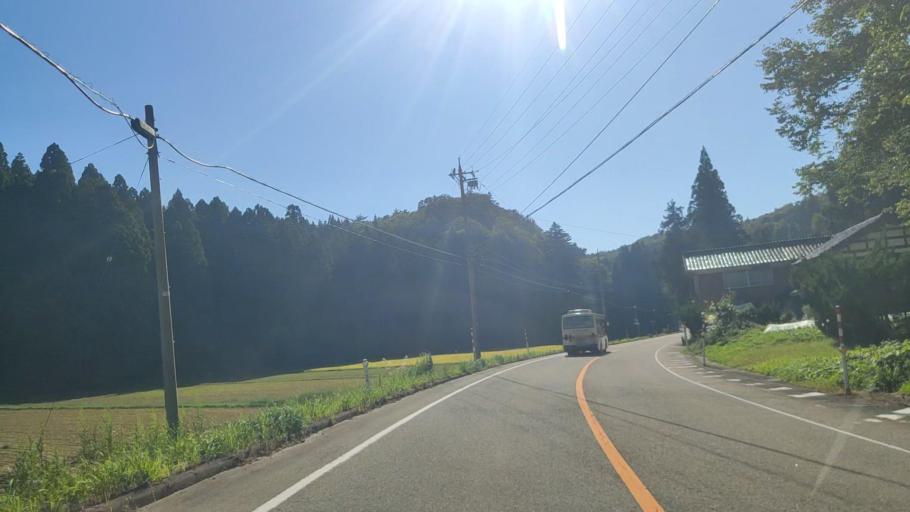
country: JP
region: Ishikawa
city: Nanao
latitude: 37.2498
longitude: 136.9982
